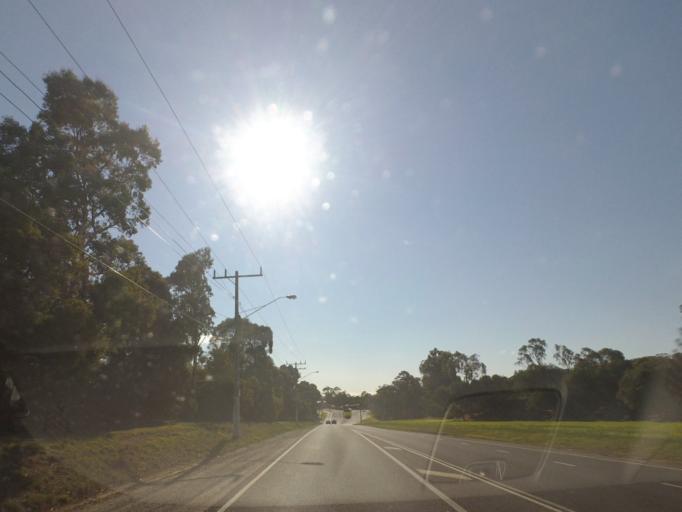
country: AU
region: Victoria
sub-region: Manningham
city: Donvale
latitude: -37.7683
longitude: 145.1832
